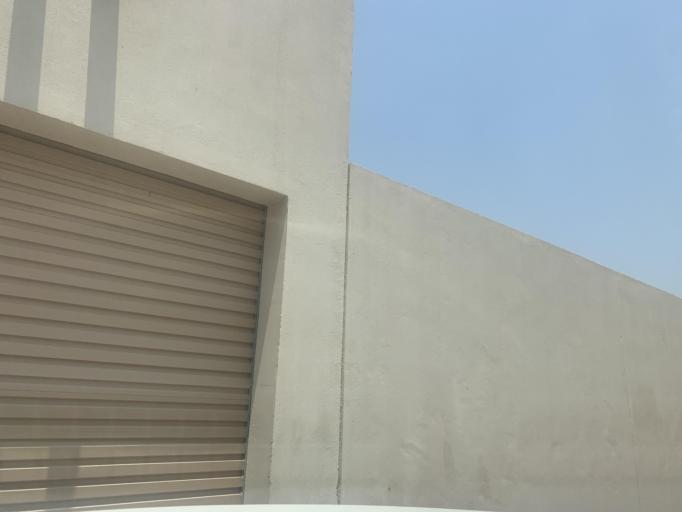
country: BH
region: Central Governorate
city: Madinat Hamad
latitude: 26.1463
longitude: 50.4633
